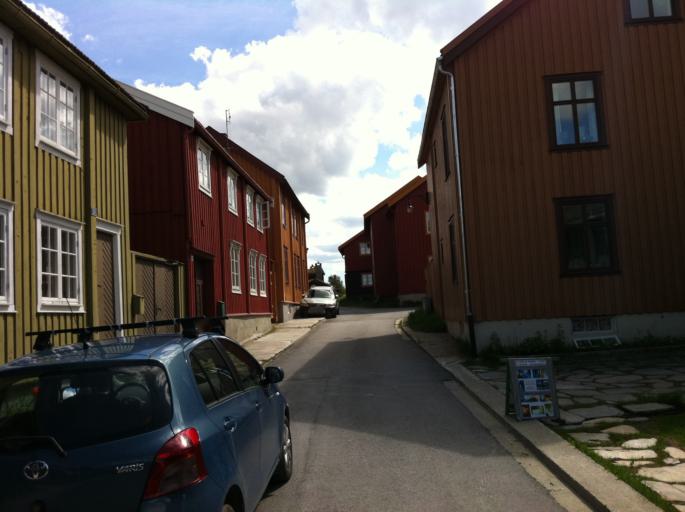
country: NO
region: Sor-Trondelag
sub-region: Roros
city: Roros
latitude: 62.5754
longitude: 11.3907
